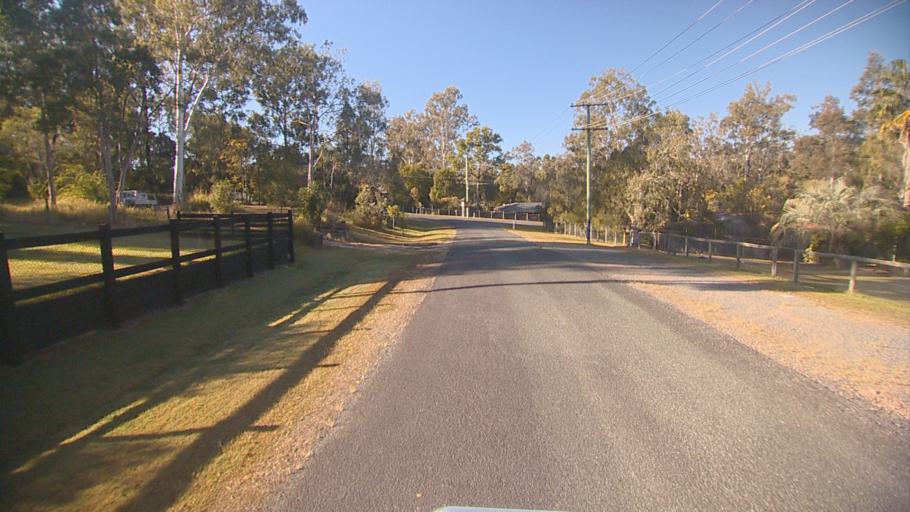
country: AU
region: Queensland
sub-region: Logan
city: North Maclean
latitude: -27.7451
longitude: 153.0166
